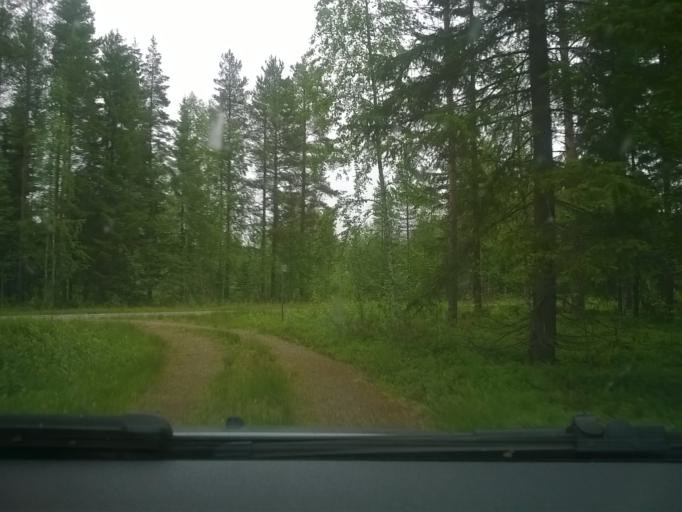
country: FI
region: Kainuu
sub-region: Kehys-Kainuu
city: Kuhmo
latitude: 64.4514
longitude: 29.7237
